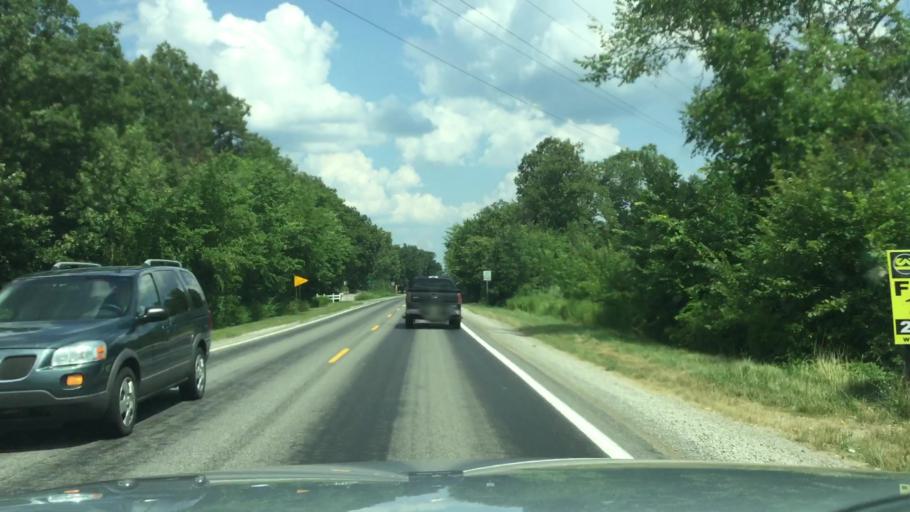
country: US
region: Michigan
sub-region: Washtenaw County
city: Ypsilanti
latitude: 42.2032
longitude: -83.5941
